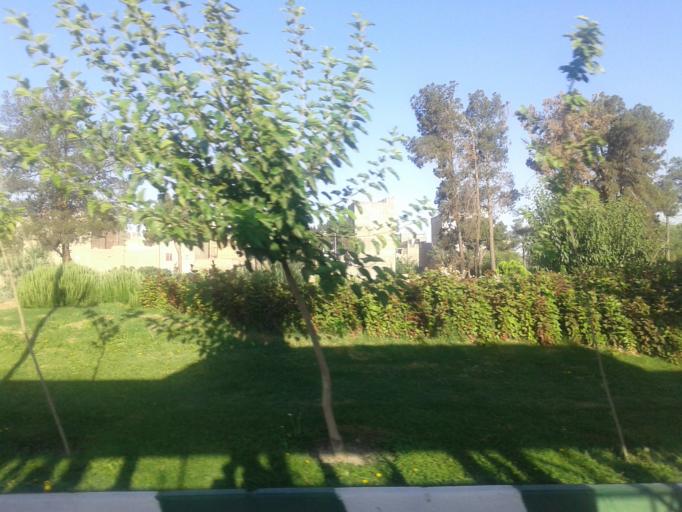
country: IR
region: Tehran
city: Rey
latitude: 35.6231
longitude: 51.3616
